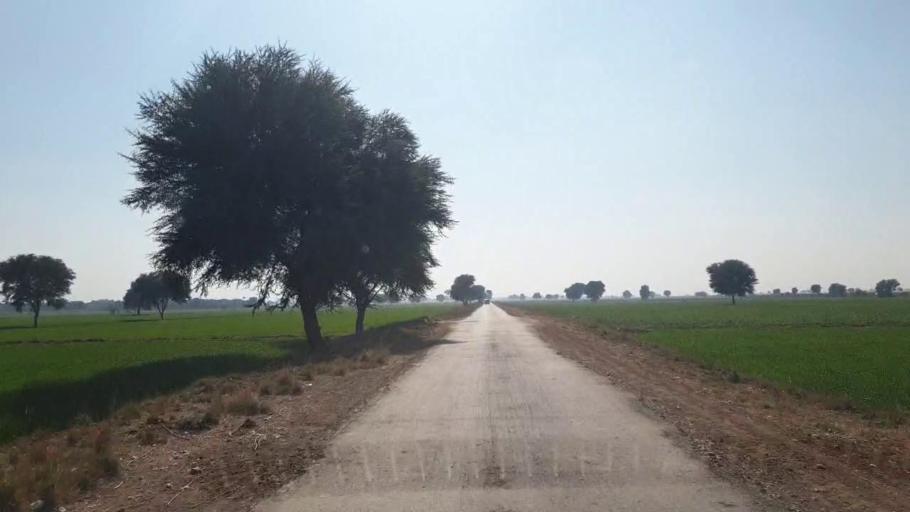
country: PK
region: Sindh
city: Shahpur Chakar
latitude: 26.1128
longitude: 68.6288
